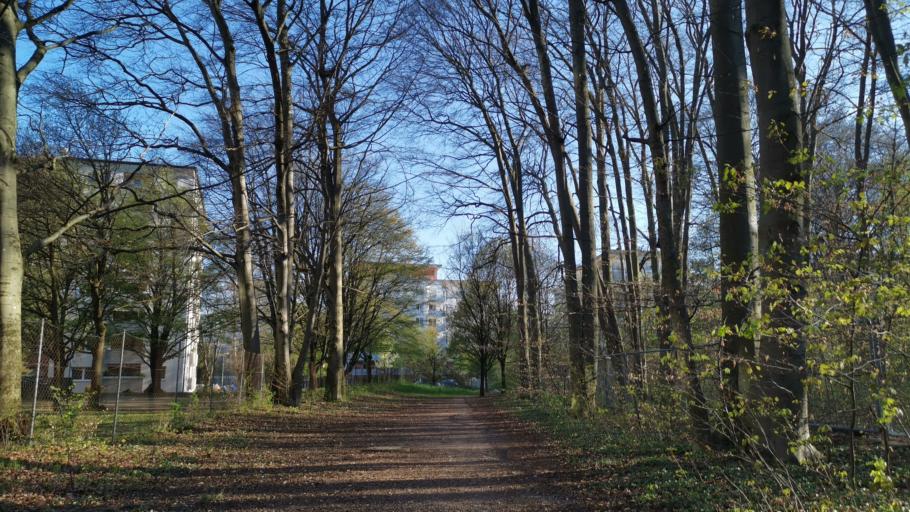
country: DE
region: Bavaria
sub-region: Upper Bavaria
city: Pullach im Isartal
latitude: 48.0924
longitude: 11.5247
